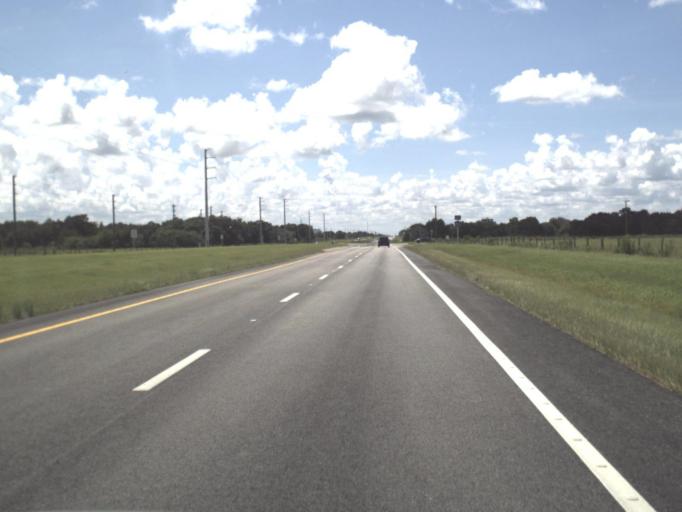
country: US
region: Florida
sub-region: Charlotte County
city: Harbour Heights
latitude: 27.0707
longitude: -81.9584
